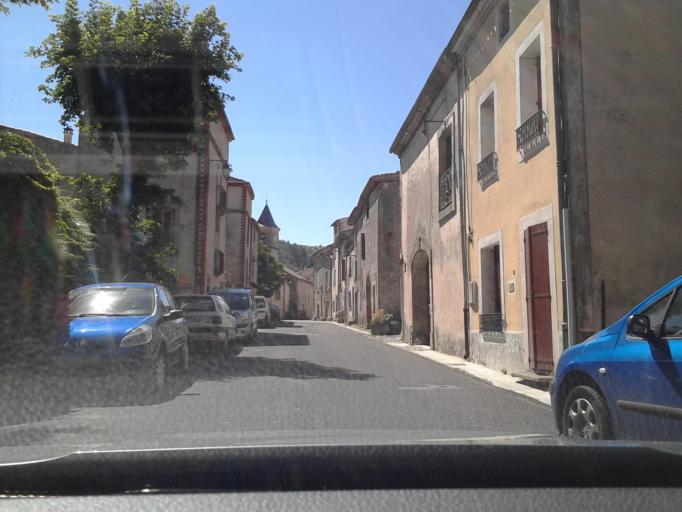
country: FR
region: Languedoc-Roussillon
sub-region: Departement de l'Herault
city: Montpeyroux
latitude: 43.7899
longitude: 3.4595
